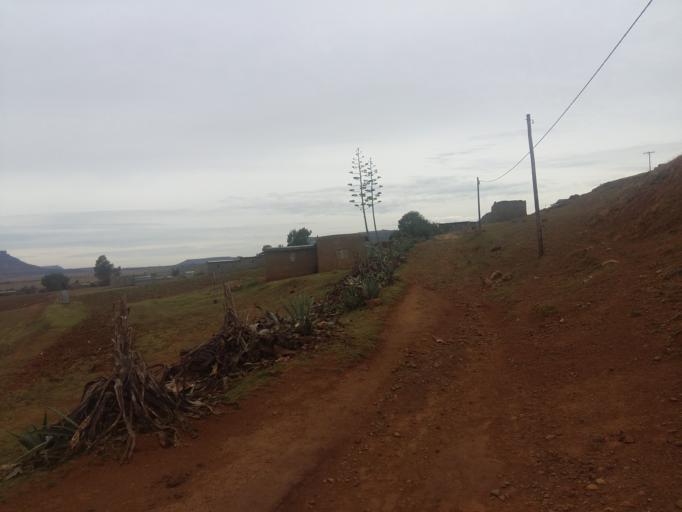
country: LS
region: Mafeteng
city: Mafeteng
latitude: -29.7038
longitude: 27.4322
